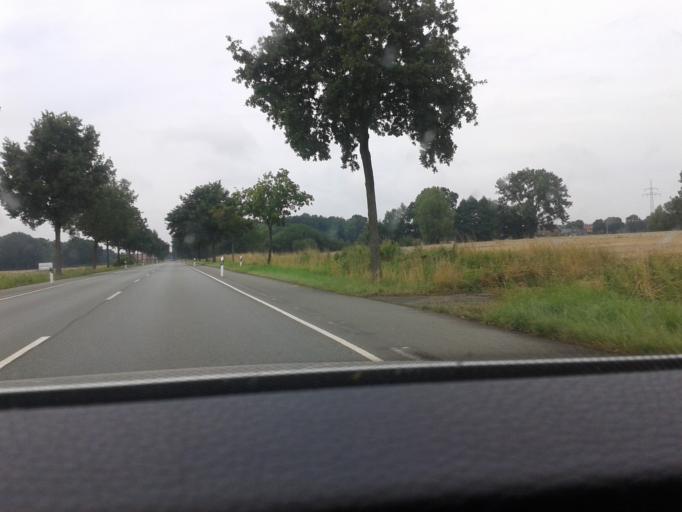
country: DE
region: Lower Saxony
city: Osloss
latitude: 52.4673
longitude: 10.6986
